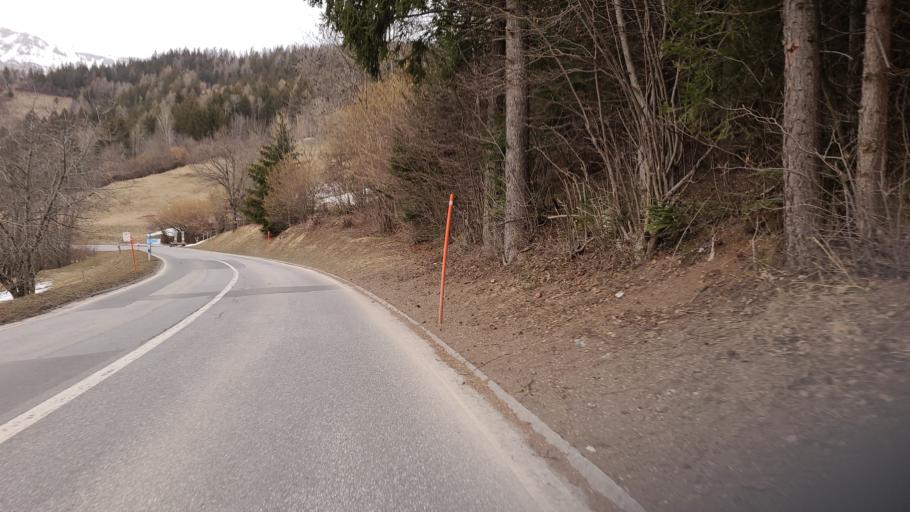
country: CH
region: Valais
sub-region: Sierre District
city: Lens
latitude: 46.2864
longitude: 7.4422
